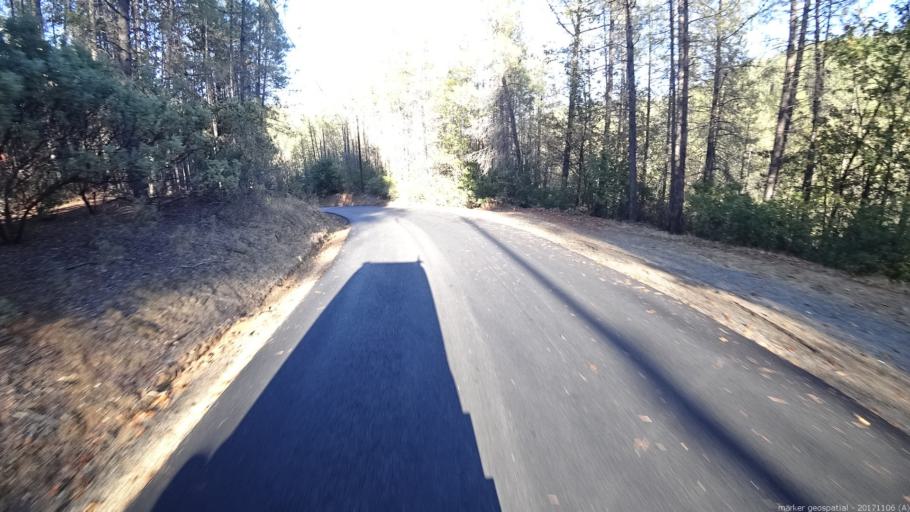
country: US
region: California
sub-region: Shasta County
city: Shasta
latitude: 40.5793
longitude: -122.4899
